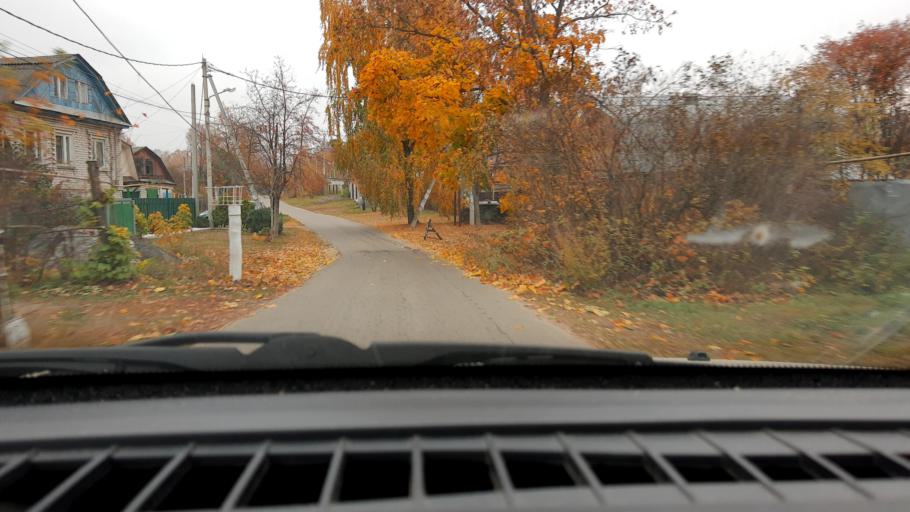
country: RU
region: Nizjnij Novgorod
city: Gorbatovka
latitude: 56.2106
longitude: 43.7584
